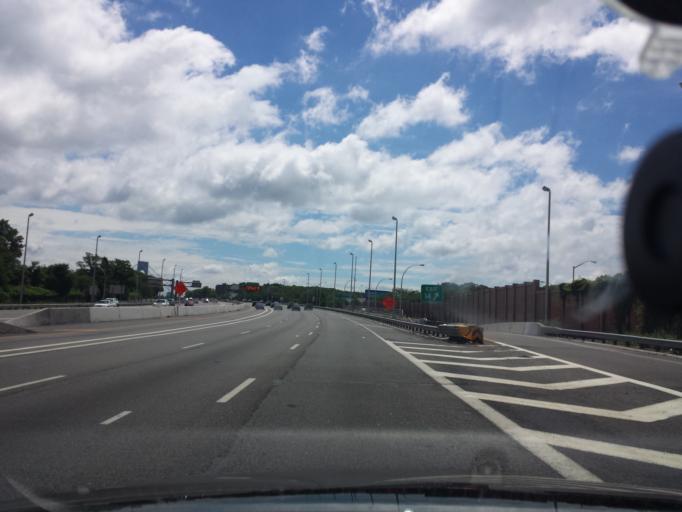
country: US
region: New Jersey
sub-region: Hudson County
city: Bayonne
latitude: 40.6070
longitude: -74.0859
